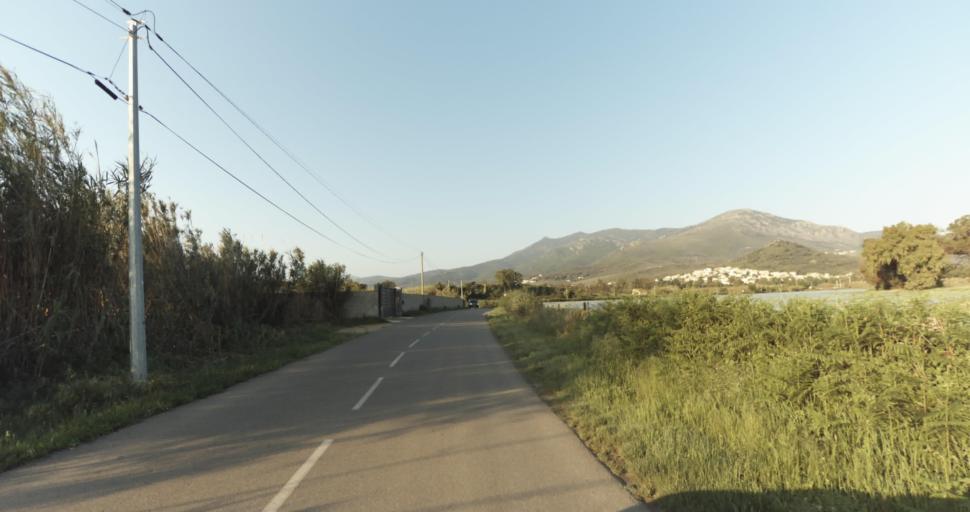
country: FR
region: Corsica
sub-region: Departement de la Haute-Corse
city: Biguglia
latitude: 42.6121
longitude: 9.4429
